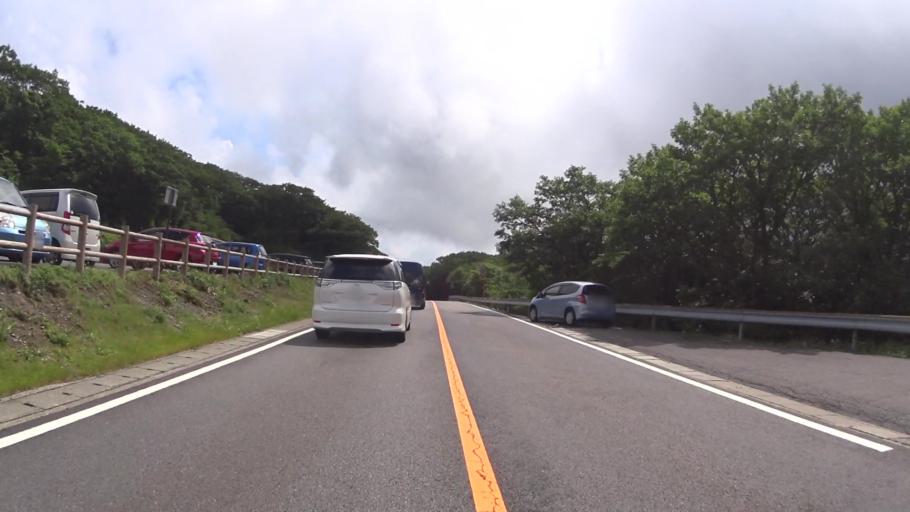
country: JP
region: Oita
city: Tsukawaki
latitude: 33.0957
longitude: 131.2073
